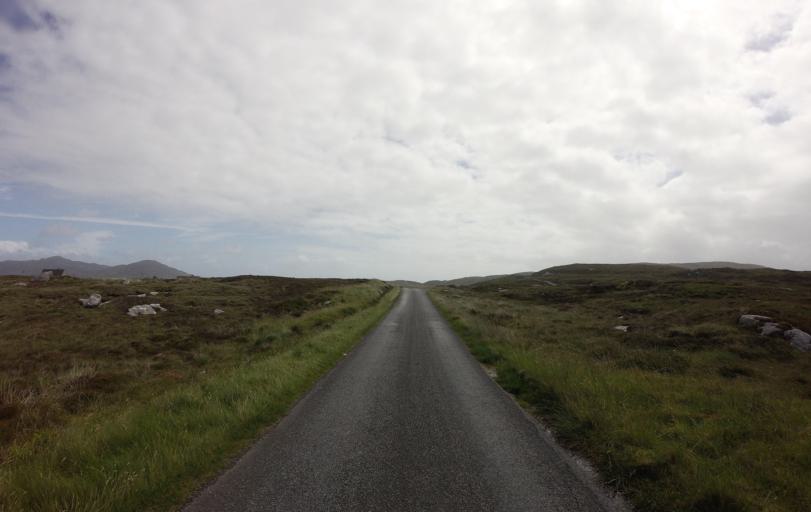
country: GB
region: Scotland
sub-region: Eilean Siar
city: Isle of South Uist
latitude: 57.1379
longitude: -7.3506
